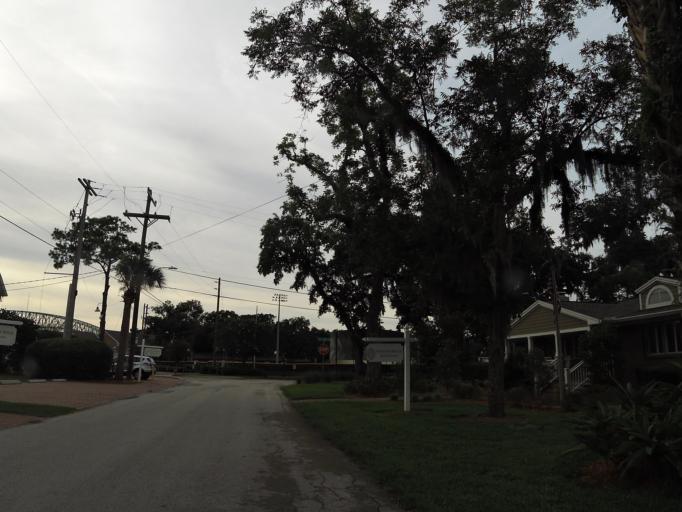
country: US
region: Florida
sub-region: Duval County
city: Jacksonville
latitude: 30.3111
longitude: -81.6201
